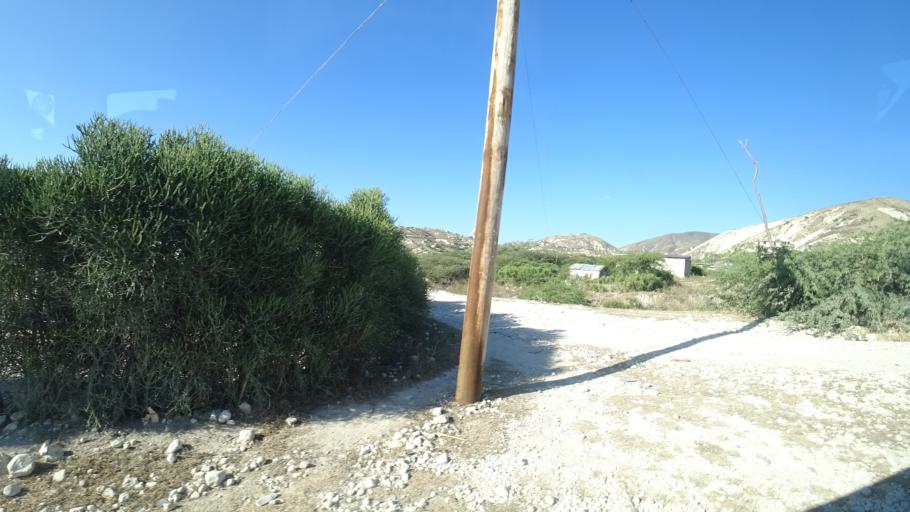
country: HT
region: Ouest
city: Croix des Bouquets
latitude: 18.6733
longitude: -72.2421
